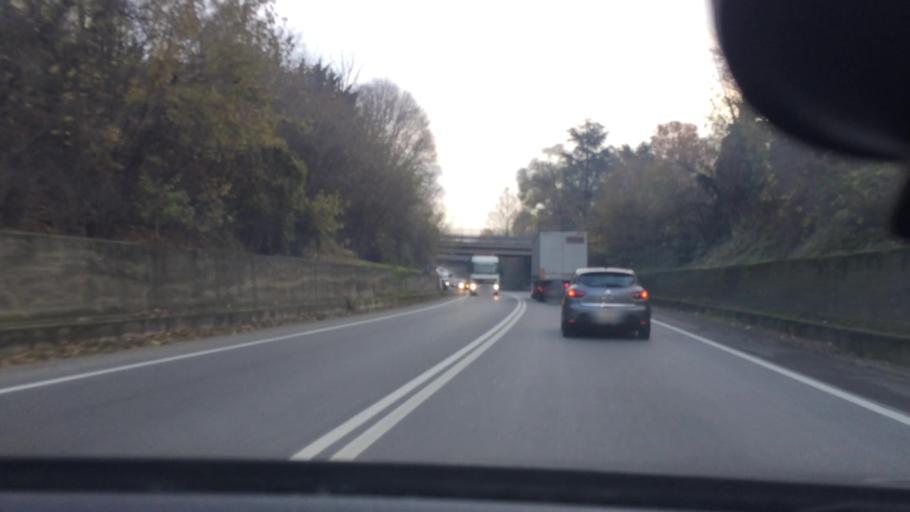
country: IT
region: Lombardy
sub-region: Provincia di Monza e Brianza
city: Bovisio-Masciago
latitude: 45.6042
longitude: 9.1440
